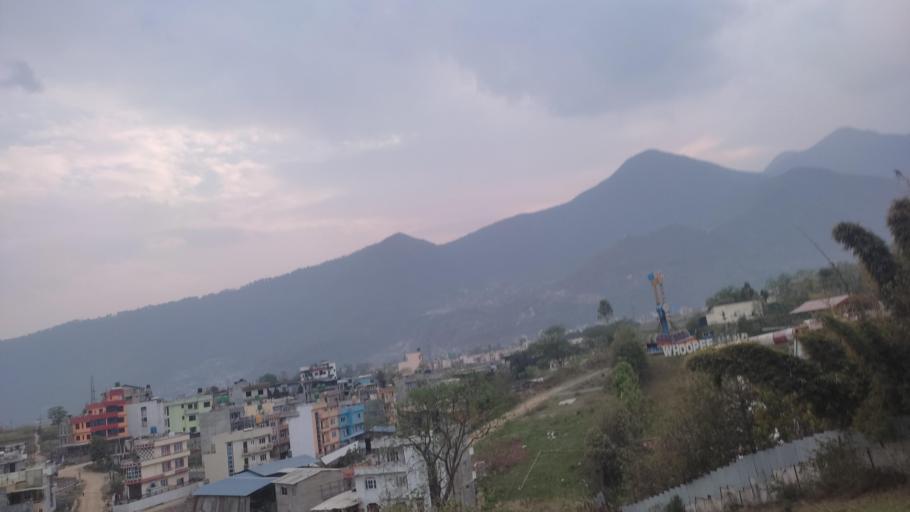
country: NP
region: Central Region
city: Kirtipur
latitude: 27.6616
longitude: 85.2877
